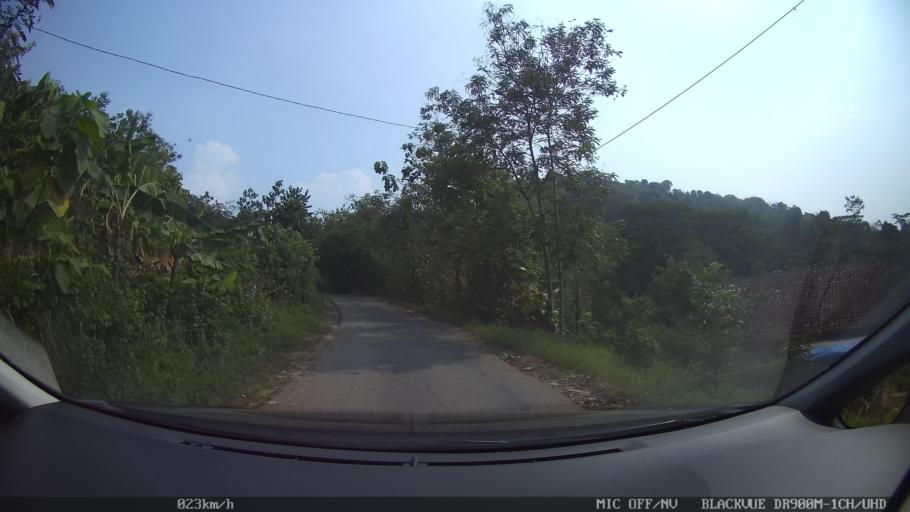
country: ID
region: Lampung
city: Pringsewu
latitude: -5.3847
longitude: 104.9935
